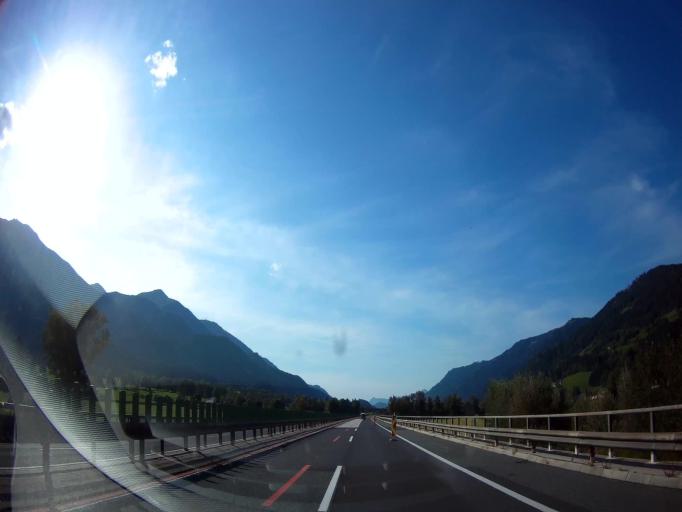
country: AT
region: Styria
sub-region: Politischer Bezirk Liezen
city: Trieben
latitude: 47.5107
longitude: 14.4343
